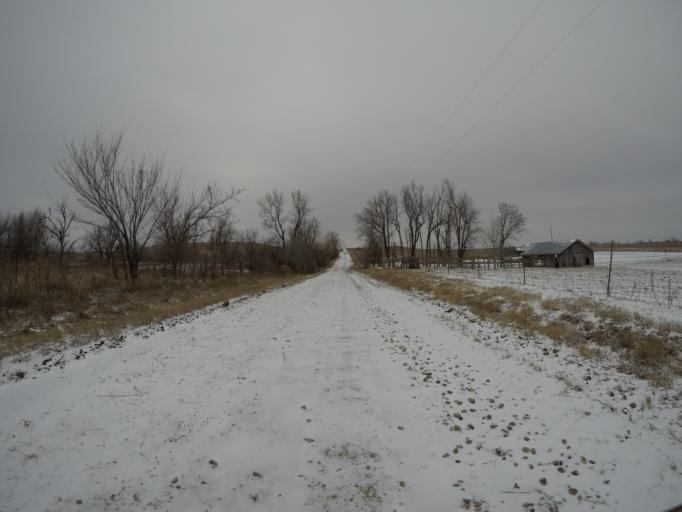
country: US
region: Kansas
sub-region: Wabaunsee County
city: Alma
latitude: 38.8646
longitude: -96.1134
